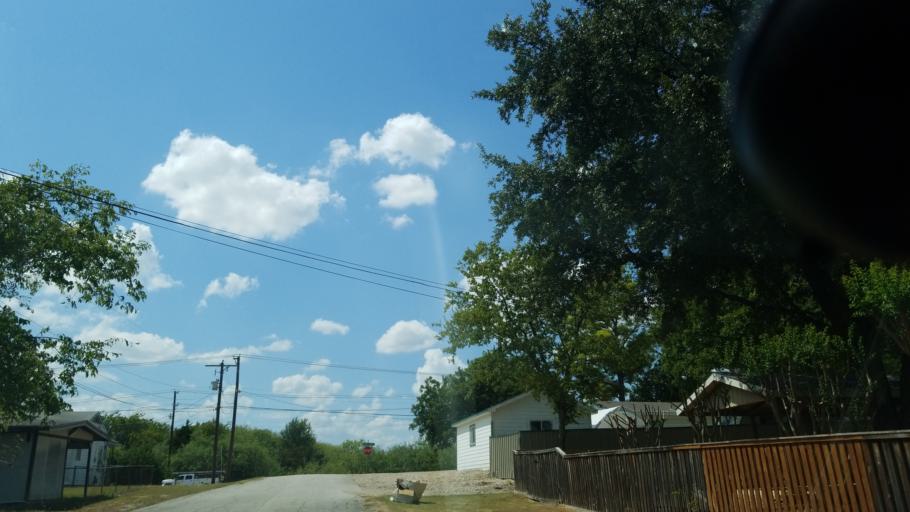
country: US
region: Texas
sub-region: Dallas County
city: Grand Prairie
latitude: 32.7265
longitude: -96.9933
